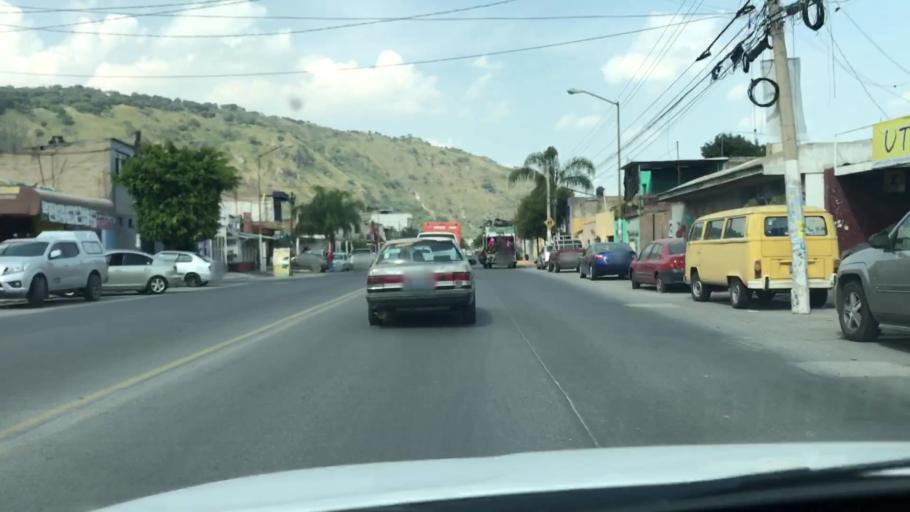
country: MX
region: Jalisco
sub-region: Tlajomulco de Zuniga
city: Palomar
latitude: 20.6422
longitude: -103.4609
